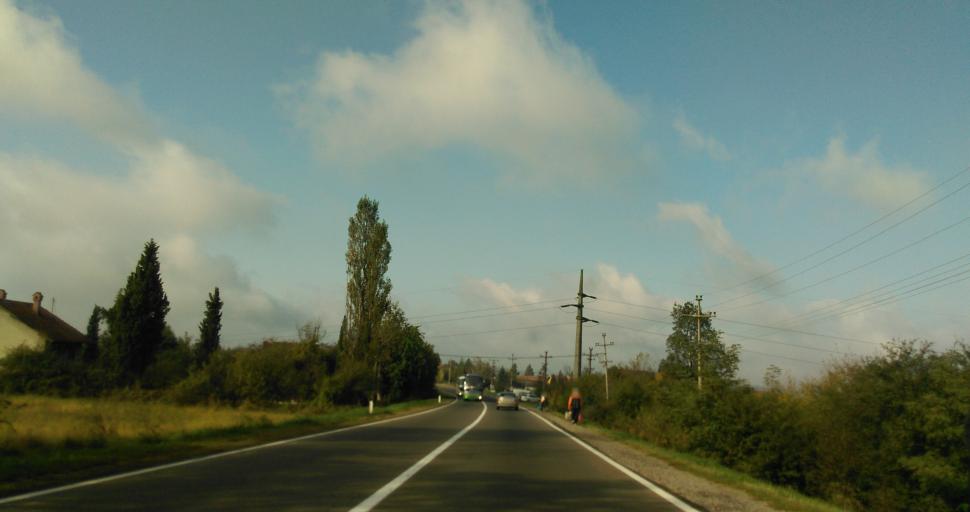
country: RS
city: Vranic
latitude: 44.5814
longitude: 20.3278
